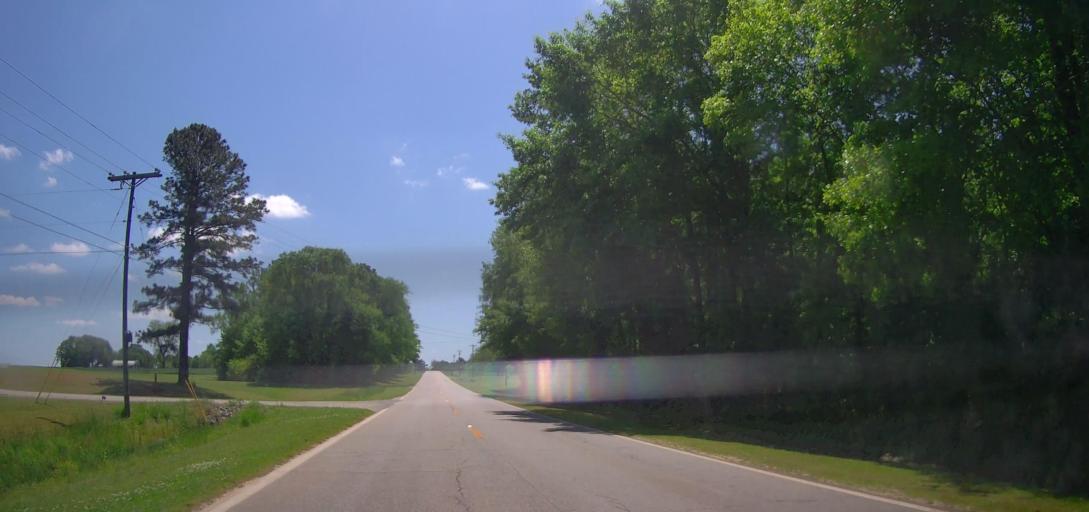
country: US
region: Georgia
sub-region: Jones County
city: Gray
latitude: 33.0455
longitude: -83.5929
